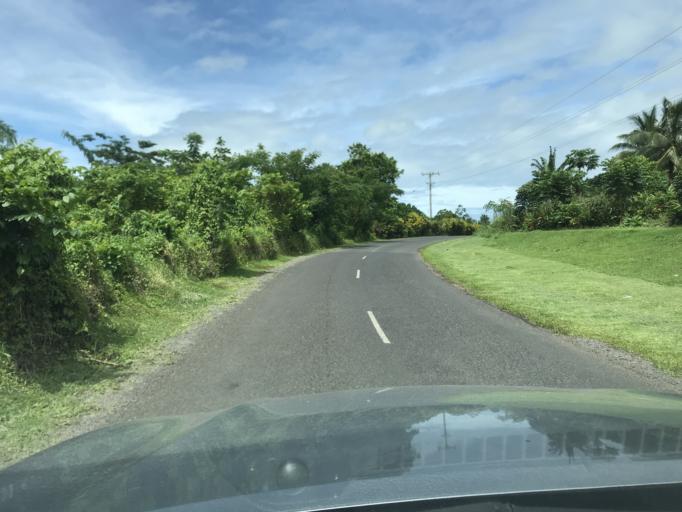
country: WS
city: Fasito`outa
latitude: -13.8578
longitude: -171.9029
